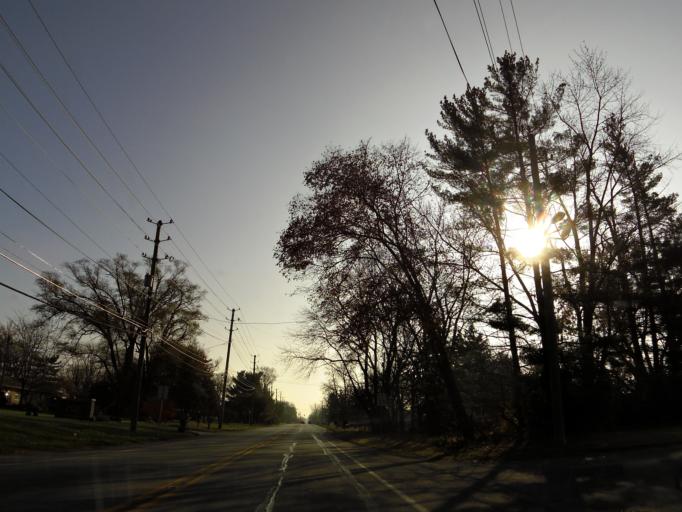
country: US
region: Indiana
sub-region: Marion County
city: Clermont
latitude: 39.8118
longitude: -86.3112
